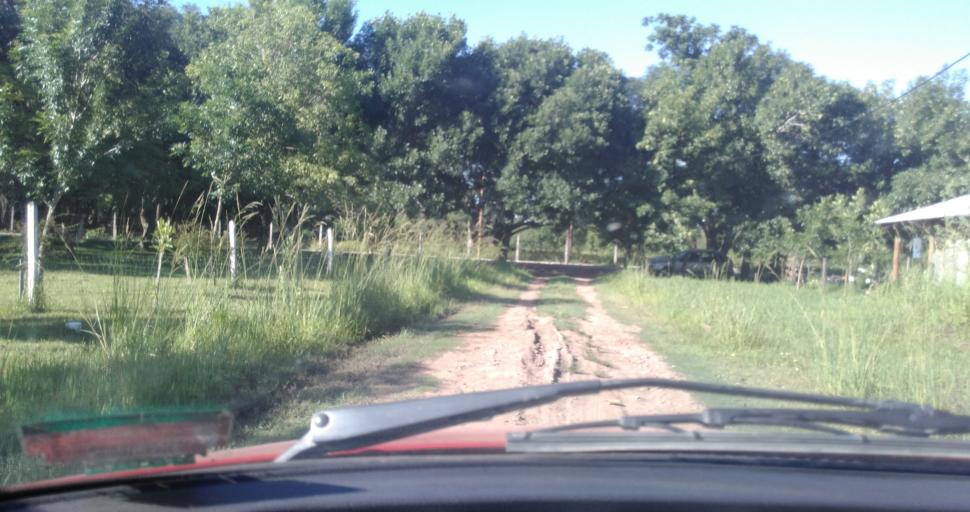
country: AR
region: Chaco
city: Resistencia
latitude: -27.4411
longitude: -58.9588
